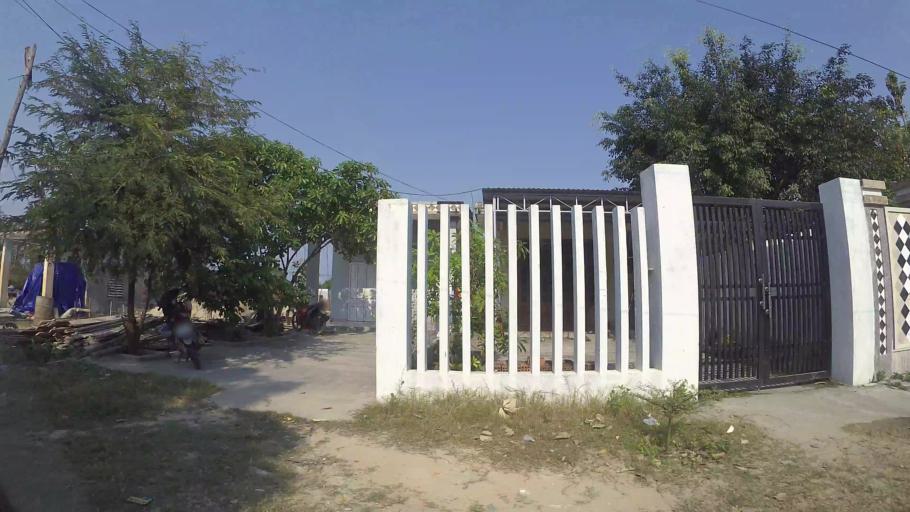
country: VN
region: Da Nang
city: Ngu Hanh Son
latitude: 15.9527
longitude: 108.2664
